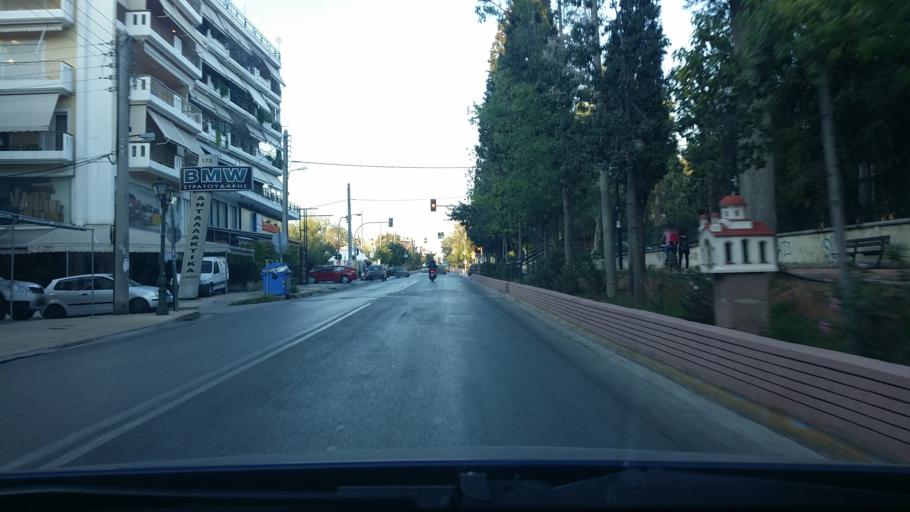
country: GR
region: Attica
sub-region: Nomarchia Athinas
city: Nea Filadelfeia
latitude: 38.0418
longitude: 23.7415
